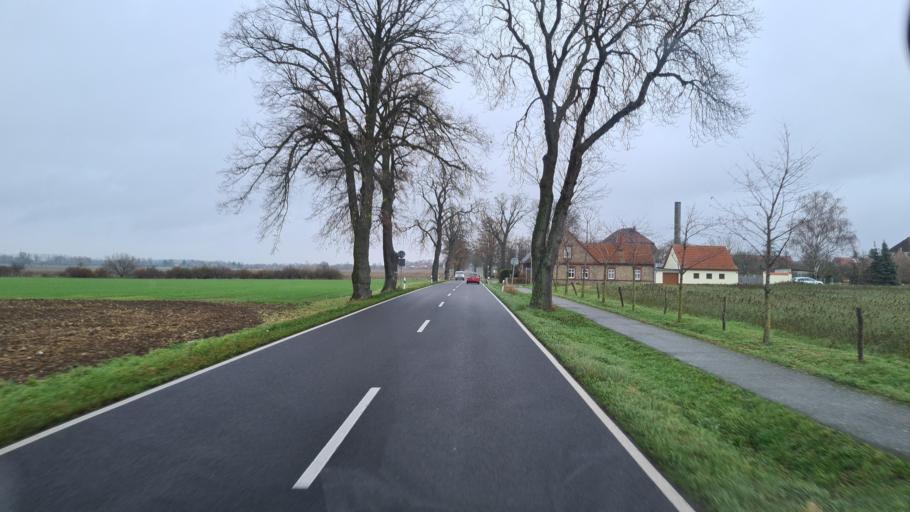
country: DE
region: Brandenburg
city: Retzow
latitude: 52.5779
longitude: 12.6241
